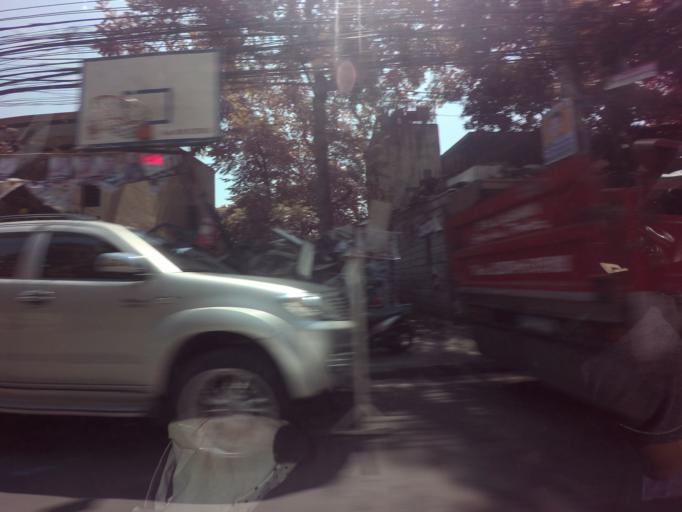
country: PH
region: Metro Manila
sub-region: City of Manila
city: Port Area
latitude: 14.5643
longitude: 120.9975
